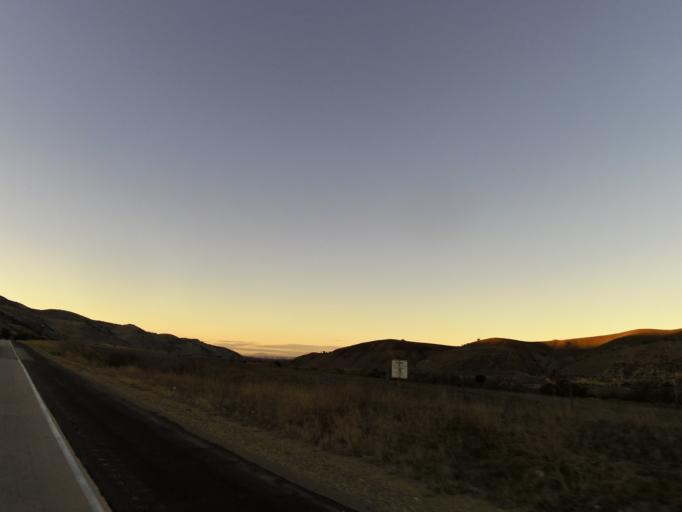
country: US
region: California
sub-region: San Luis Obispo County
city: Lake Nacimiento
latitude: 35.9132
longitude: -120.8523
